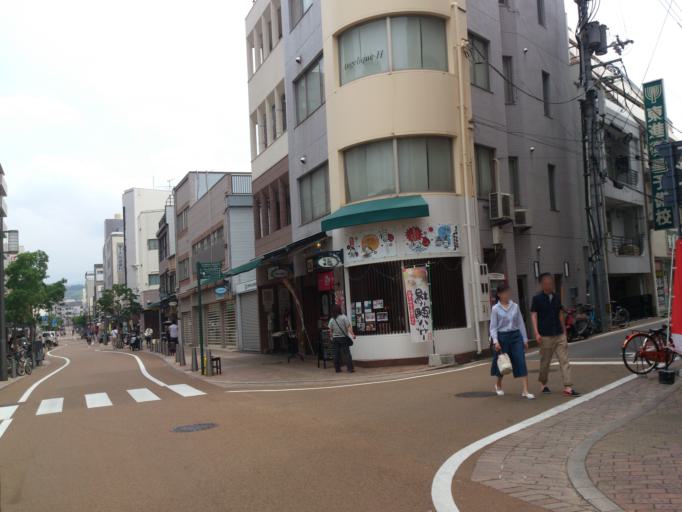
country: JP
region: Ehime
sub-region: Shikoku-chuo Shi
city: Matsuyama
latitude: 33.8422
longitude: 132.7704
